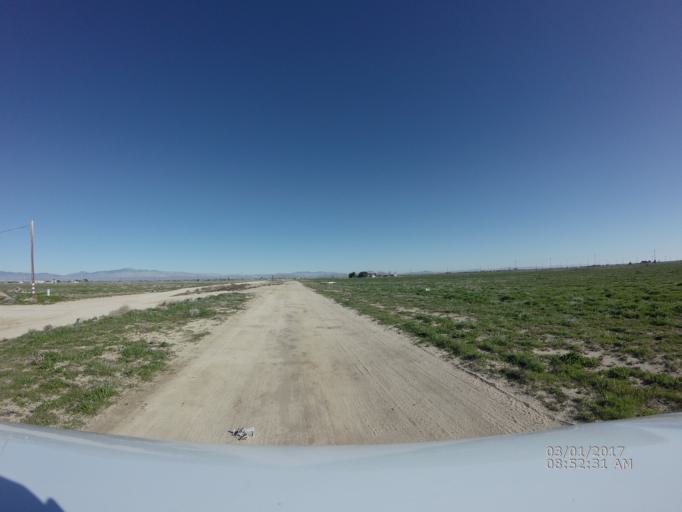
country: US
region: California
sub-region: Los Angeles County
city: Quartz Hill
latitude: 34.7292
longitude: -118.2722
